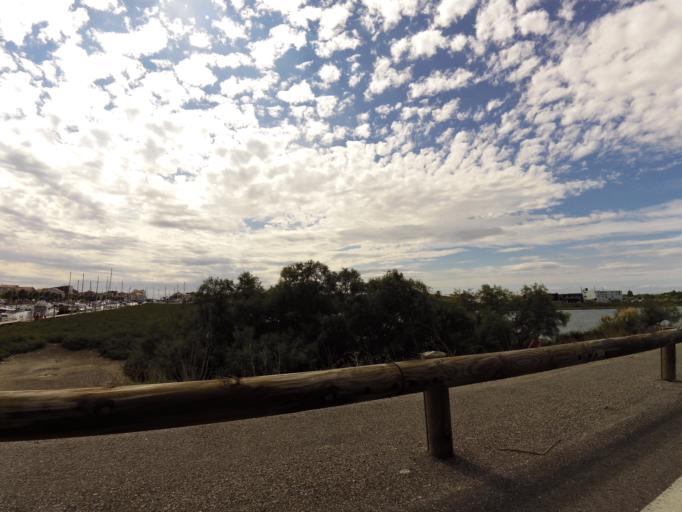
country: FR
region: Languedoc-Roussillon
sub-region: Departement du Gard
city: Le Grau-du-Roi
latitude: 43.5405
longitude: 4.1426
